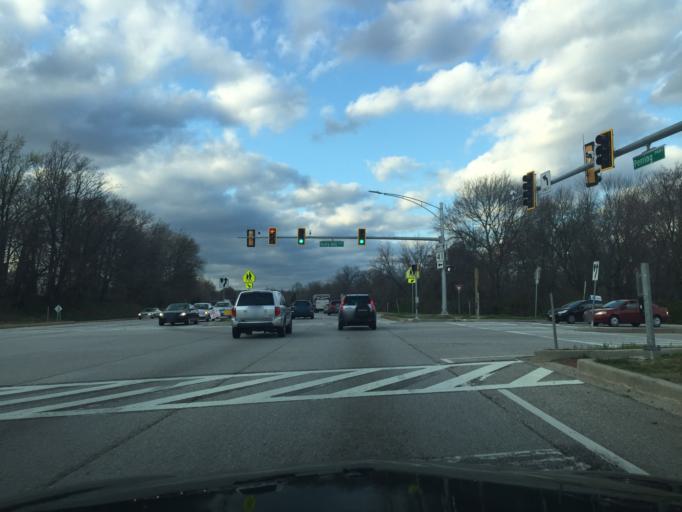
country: US
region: Maryland
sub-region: Baltimore County
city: Parkville
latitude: 39.3887
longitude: -76.5510
